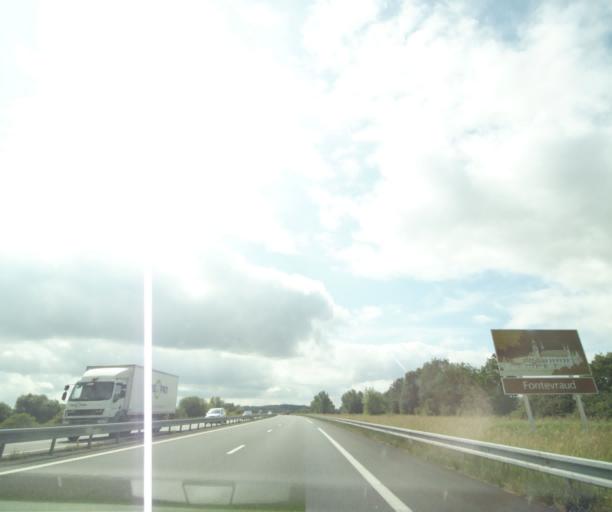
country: FR
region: Pays de la Loire
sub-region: Departement de Maine-et-Loire
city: Vivy
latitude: 47.3463
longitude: -0.0701
